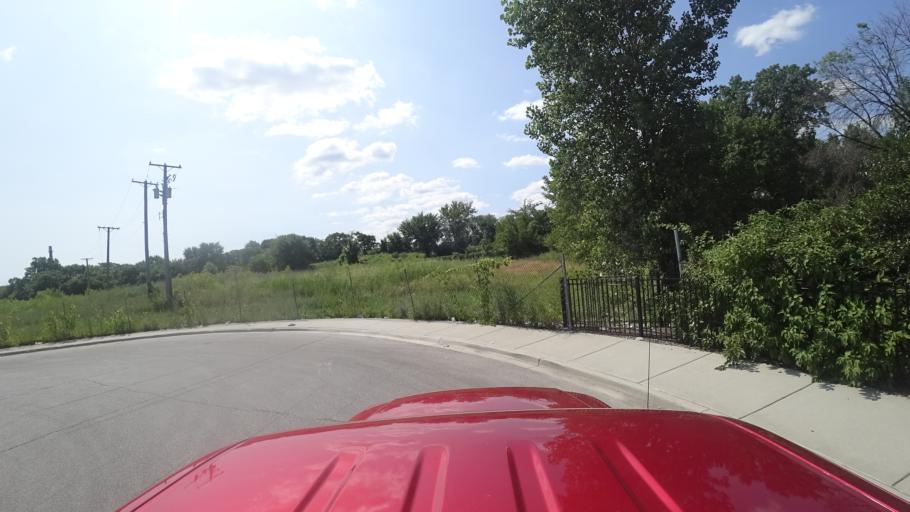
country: US
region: Illinois
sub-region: Cook County
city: Chicago
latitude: 41.8056
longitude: -87.6894
